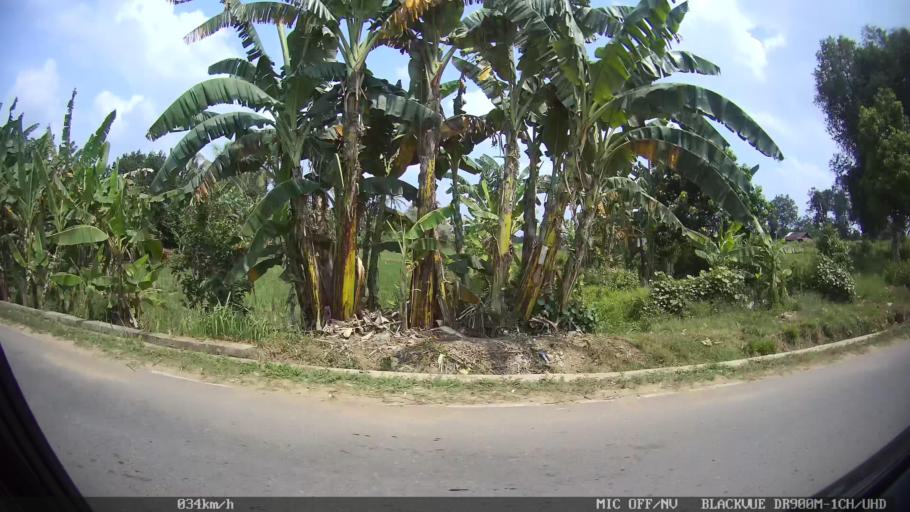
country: ID
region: Lampung
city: Pringsewu
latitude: -5.3683
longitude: 104.9678
